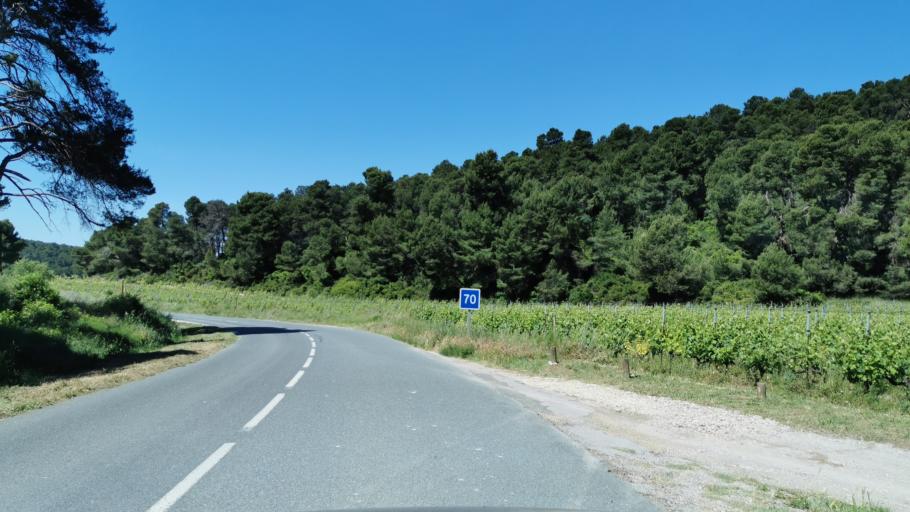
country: FR
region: Languedoc-Roussillon
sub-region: Departement de l'Aude
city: Armissan
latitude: 43.1738
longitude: 3.0775
